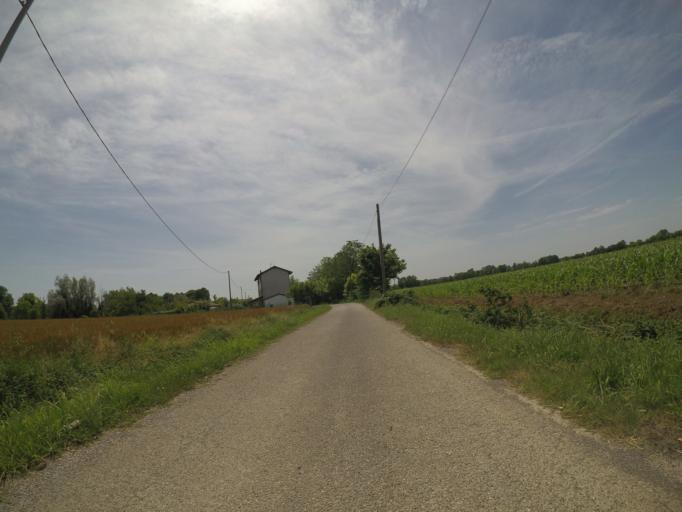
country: IT
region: Friuli Venezia Giulia
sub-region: Provincia di Udine
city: Camino al Tagliamento
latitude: 45.9035
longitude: 12.9590
